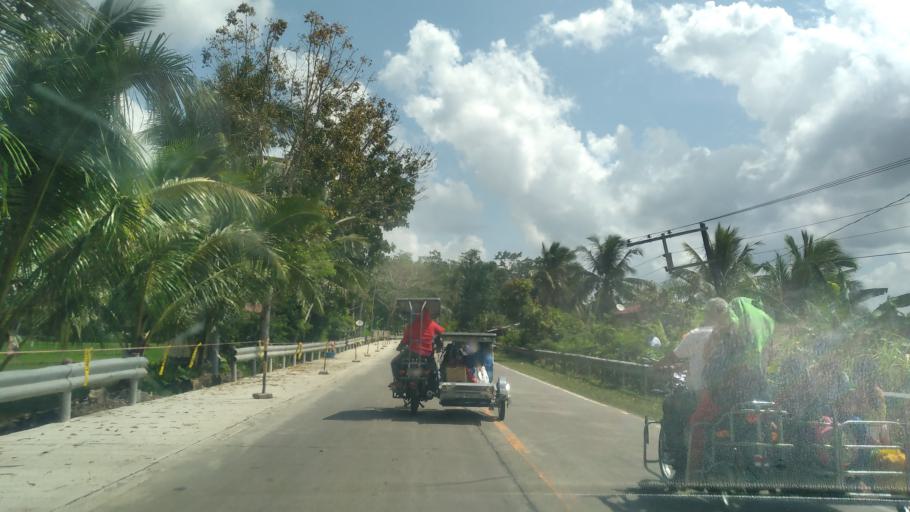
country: PH
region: Calabarzon
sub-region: Province of Quezon
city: Macalelon
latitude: 13.7570
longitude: 122.1478
